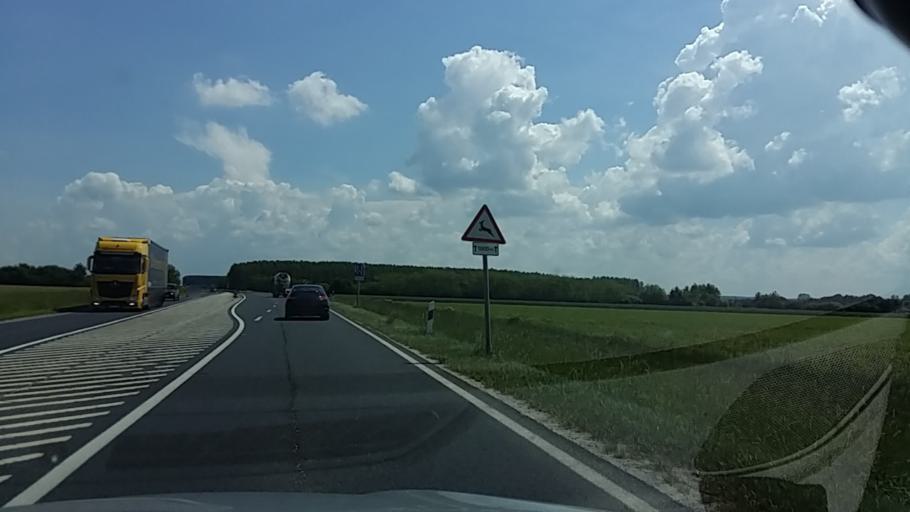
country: AT
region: Burgenland
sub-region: Politischer Bezirk Gussing
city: Heiligenbrunn
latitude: 46.9683
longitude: 16.4669
